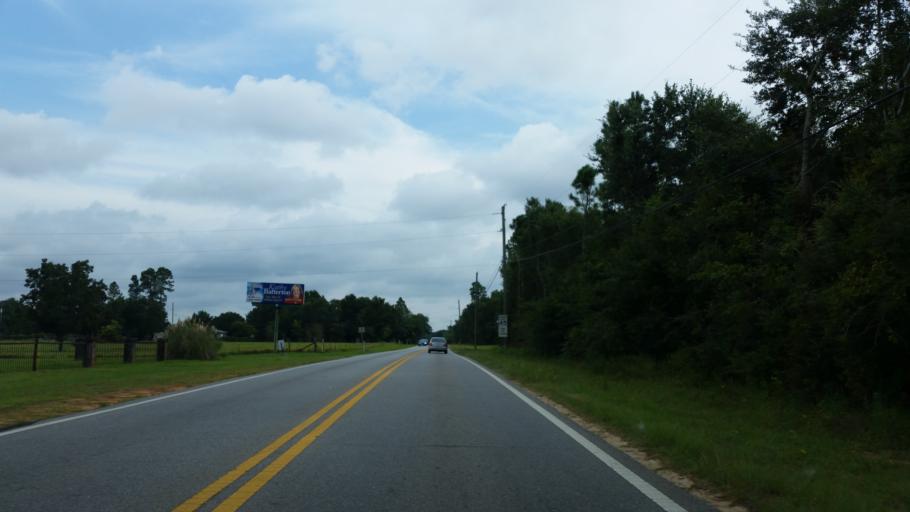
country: US
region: Florida
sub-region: Santa Rosa County
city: Wallace
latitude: 30.6467
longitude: -87.1476
